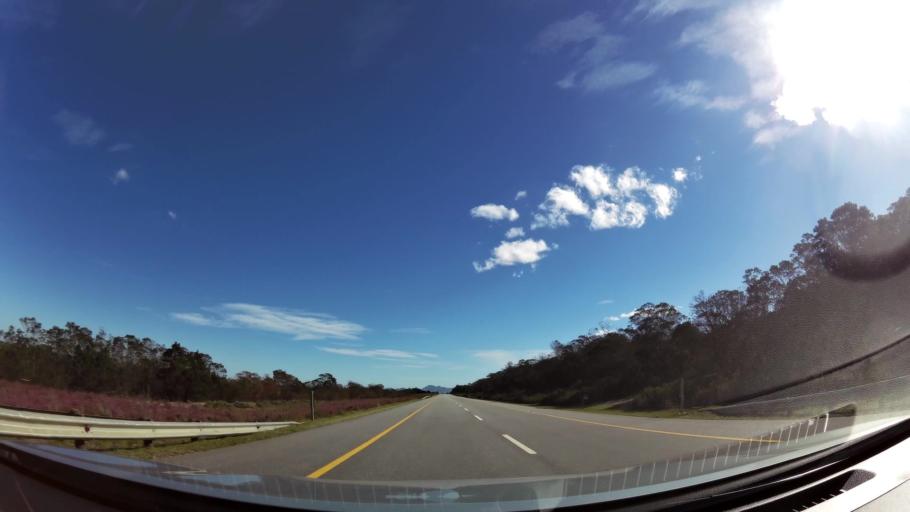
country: ZA
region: Eastern Cape
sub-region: Cacadu District Municipality
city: Kruisfontein
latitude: -33.9948
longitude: 24.7211
